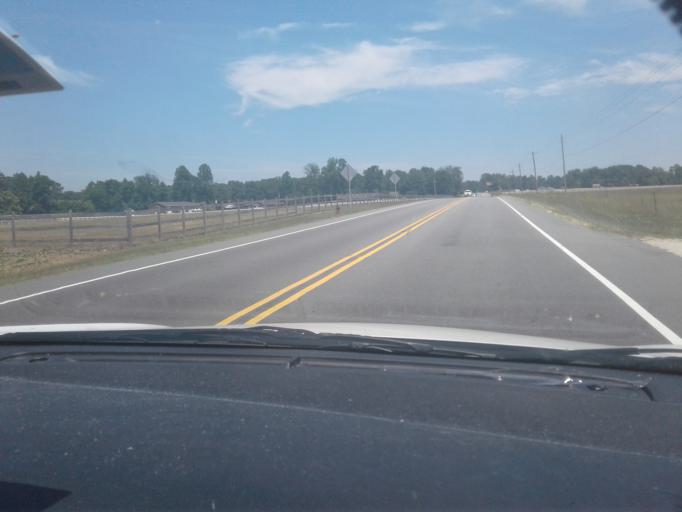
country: US
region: North Carolina
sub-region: Harnett County
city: Lillington
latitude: 35.4502
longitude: -78.8286
